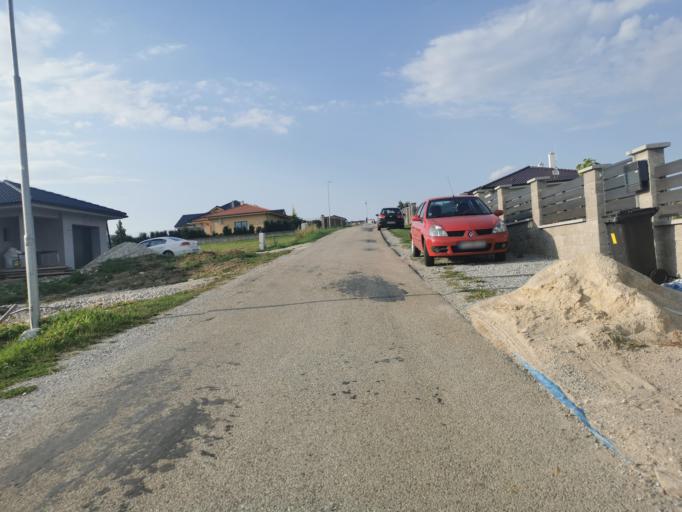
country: SK
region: Trenciansky
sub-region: Okres Myjava
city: Myjava
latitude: 48.7812
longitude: 17.5658
